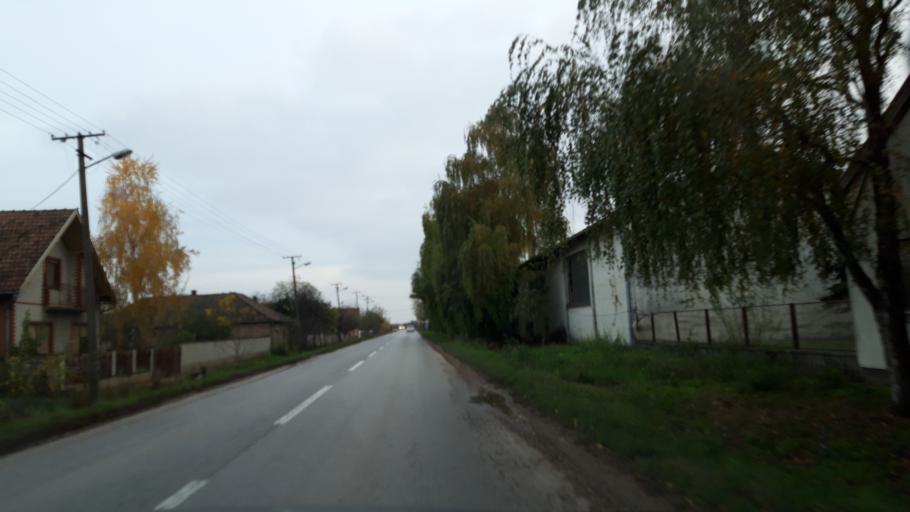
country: RS
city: Sanad
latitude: 45.9785
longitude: 20.1150
